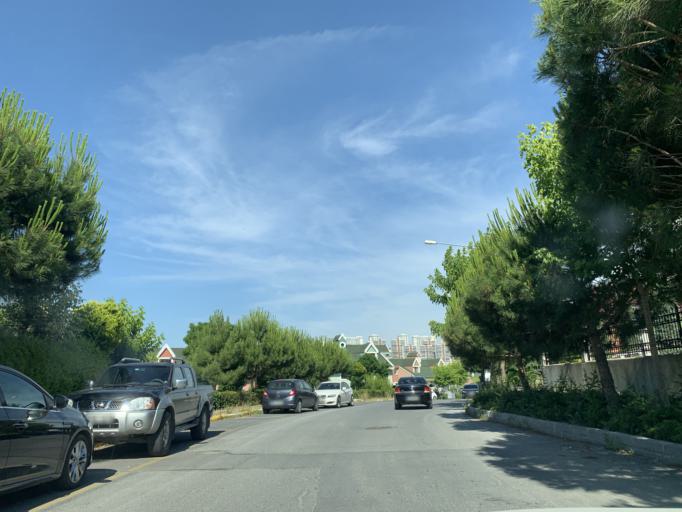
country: TR
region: Istanbul
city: Esenyurt
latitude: 41.0834
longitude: 28.6718
